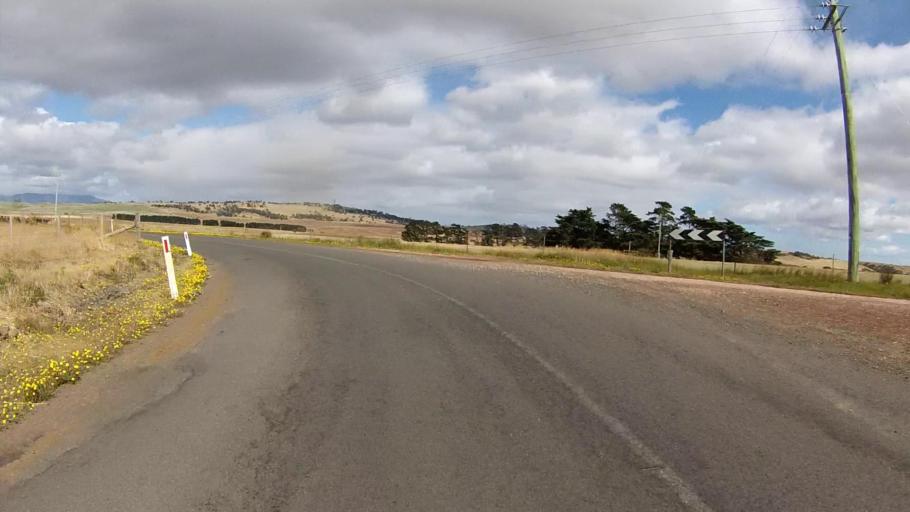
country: AU
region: Tasmania
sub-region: Northern Midlands
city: Evandale
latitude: -41.7740
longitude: 147.4587
